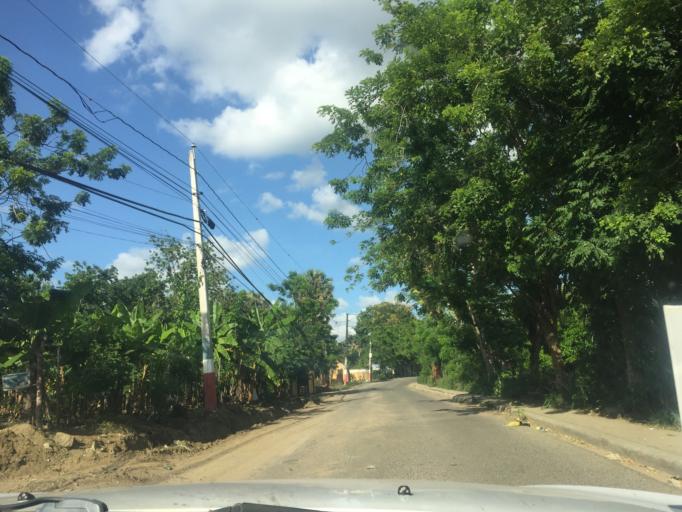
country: DO
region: Santiago
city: Tamboril
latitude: 19.4978
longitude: -70.6379
